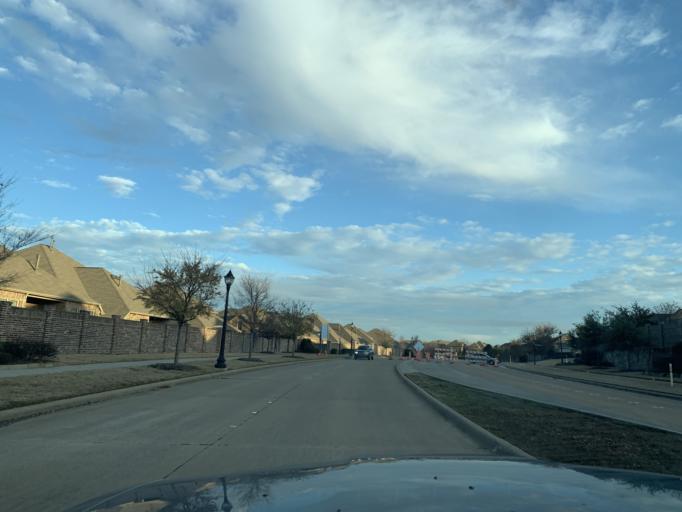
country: US
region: Texas
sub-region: Tarrant County
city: Euless
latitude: 32.8464
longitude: -97.0699
